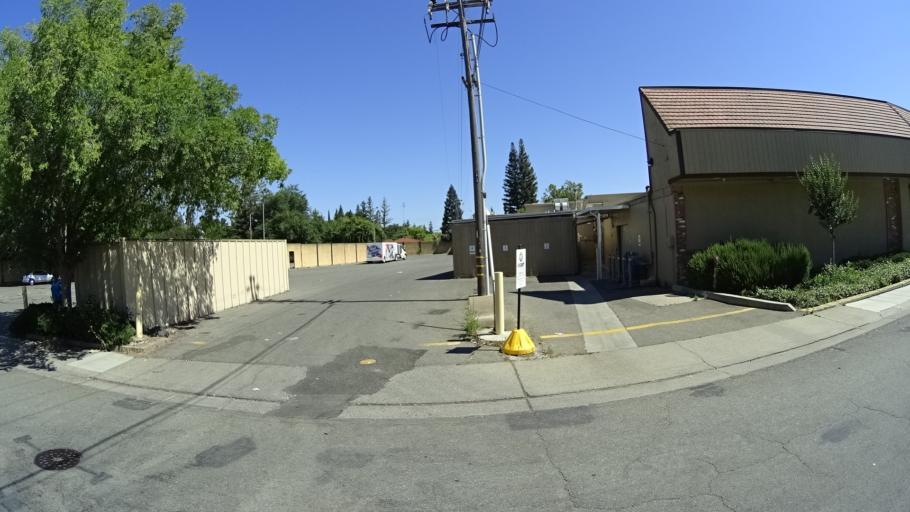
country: US
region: California
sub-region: Sacramento County
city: Parkway
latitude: 38.5302
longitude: -121.4968
